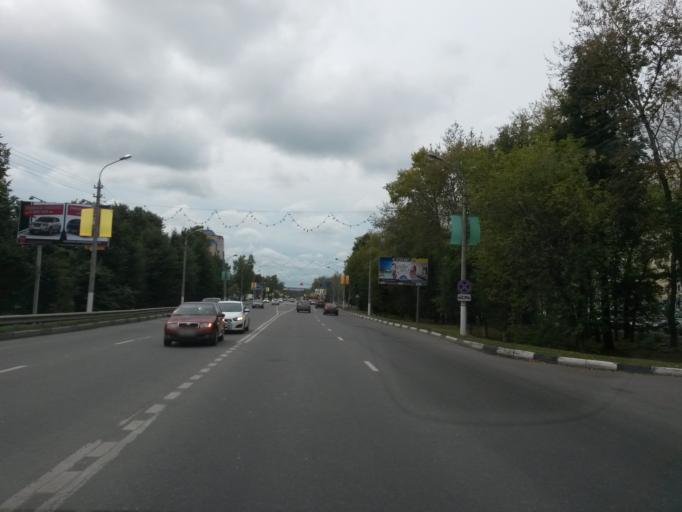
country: RU
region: Moskovskaya
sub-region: Chekhovskiy Rayon
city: Chekhov
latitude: 55.1548
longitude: 37.4622
